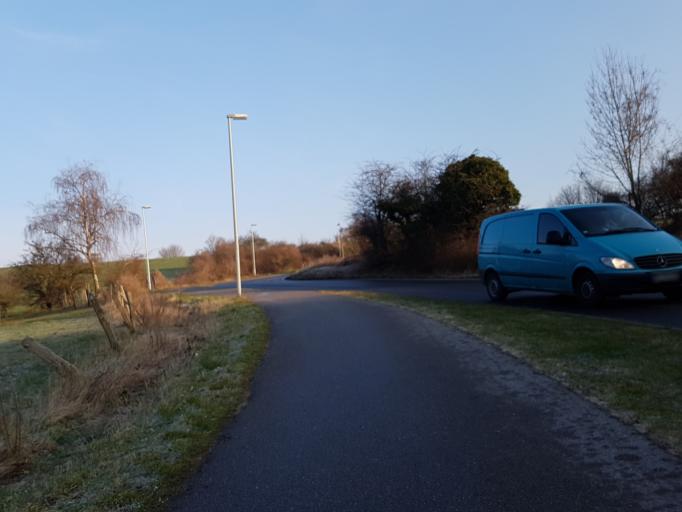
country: DE
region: North Rhine-Westphalia
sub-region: Regierungsbezirk Koln
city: Wurselen
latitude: 50.7916
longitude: 6.1571
